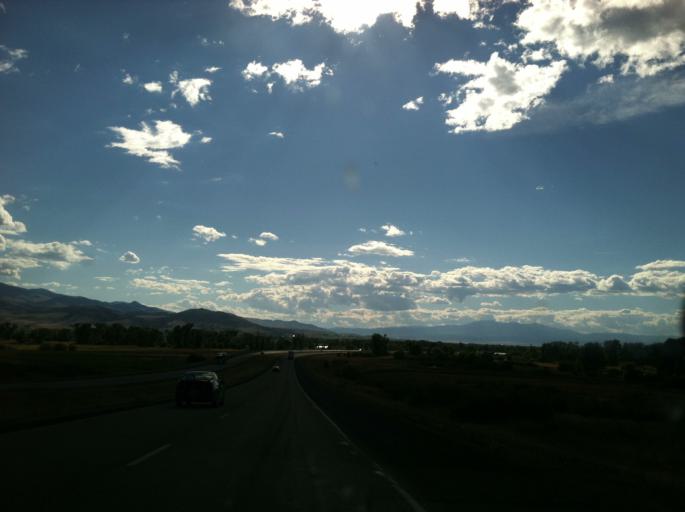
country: US
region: Montana
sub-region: Jefferson County
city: Whitehall
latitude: 45.8737
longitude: -111.9343
